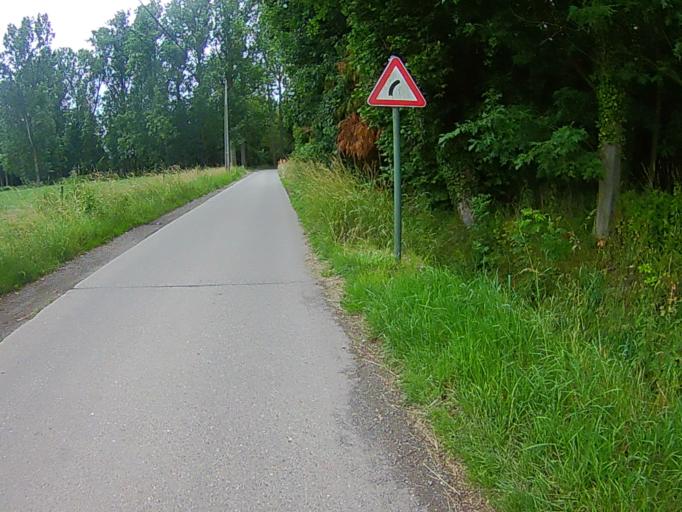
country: BE
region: Flanders
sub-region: Provincie Antwerpen
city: Ranst
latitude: 51.1630
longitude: 4.5581
